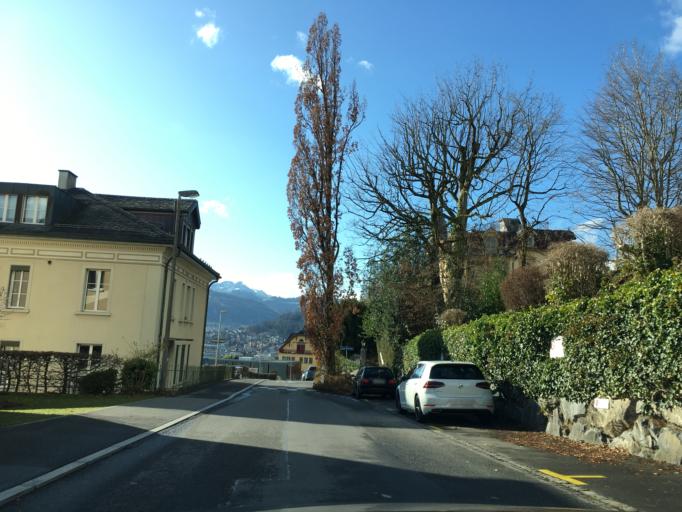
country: CH
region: Lucerne
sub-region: Lucerne-Stadt District
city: Luzern
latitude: 47.0575
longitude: 8.3226
